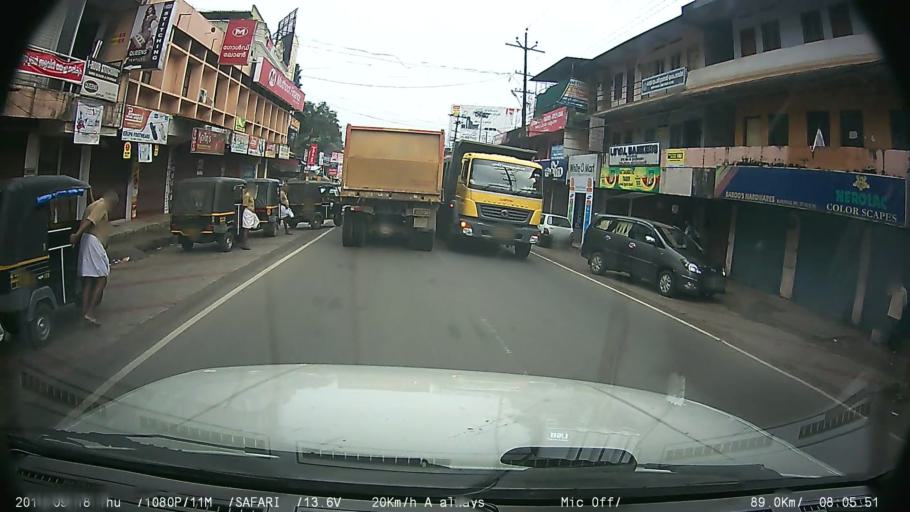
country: IN
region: Kerala
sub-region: Kottayam
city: Kottayam
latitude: 9.5874
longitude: 76.5828
